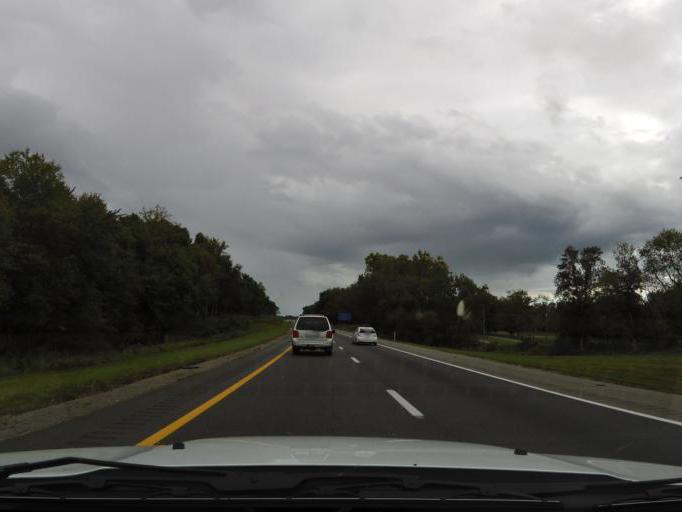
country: US
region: Kentucky
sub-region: Laurel County
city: North Corbin
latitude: 37.0243
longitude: -84.0983
